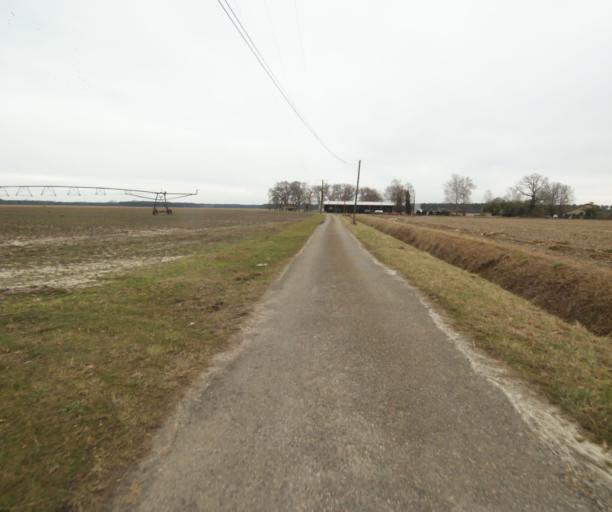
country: FR
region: Aquitaine
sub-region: Departement des Landes
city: Gabarret
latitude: 44.0155
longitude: -0.0136
